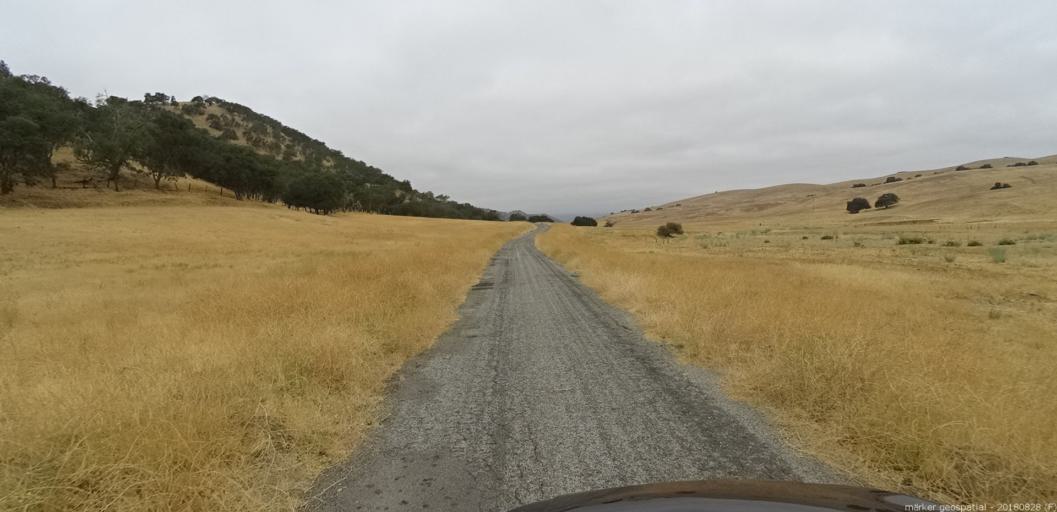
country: US
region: California
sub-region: San Luis Obispo County
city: San Miguel
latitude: 35.9412
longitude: -120.7770
